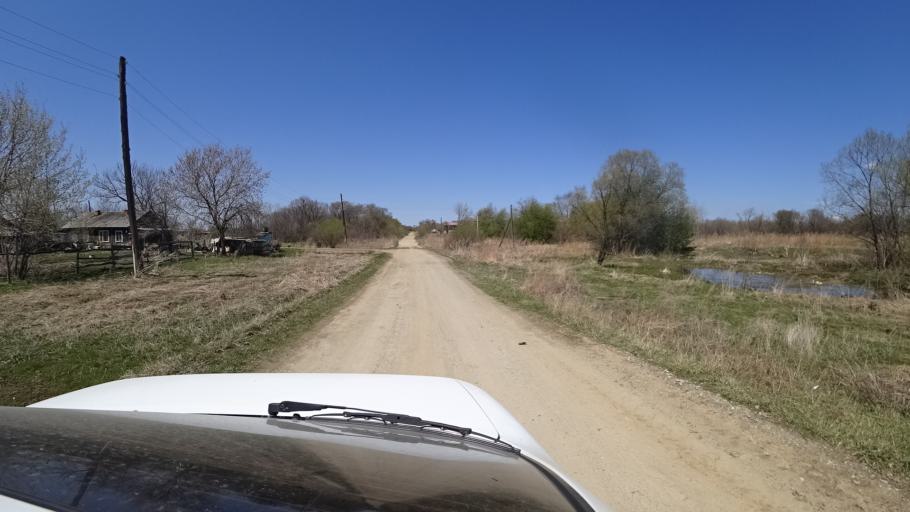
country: RU
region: Primorskiy
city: Dal'nerechensk
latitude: 45.8039
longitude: 133.7669
